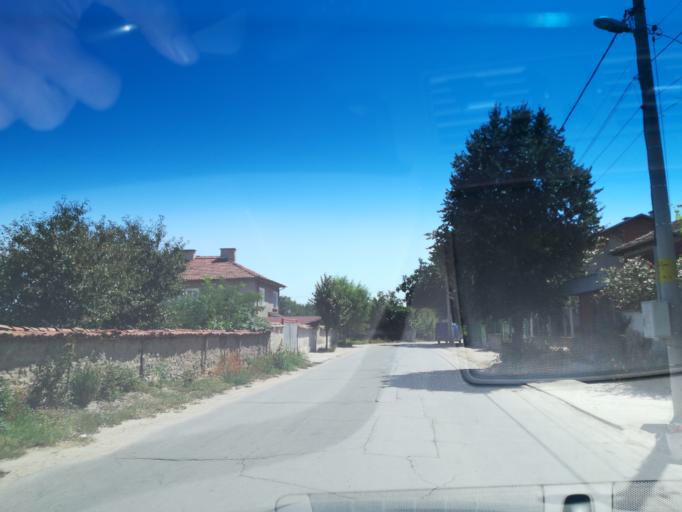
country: BG
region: Pazardzhik
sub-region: Obshtina Pazardzhik
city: Pazardzhik
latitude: 42.2764
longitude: 24.3961
